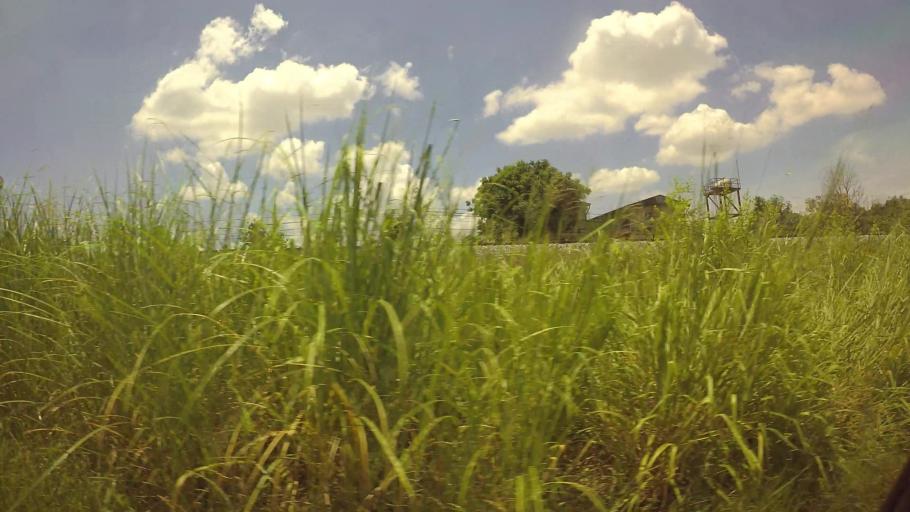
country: TH
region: Chon Buri
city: Si Racha
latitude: 13.1200
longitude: 100.9441
